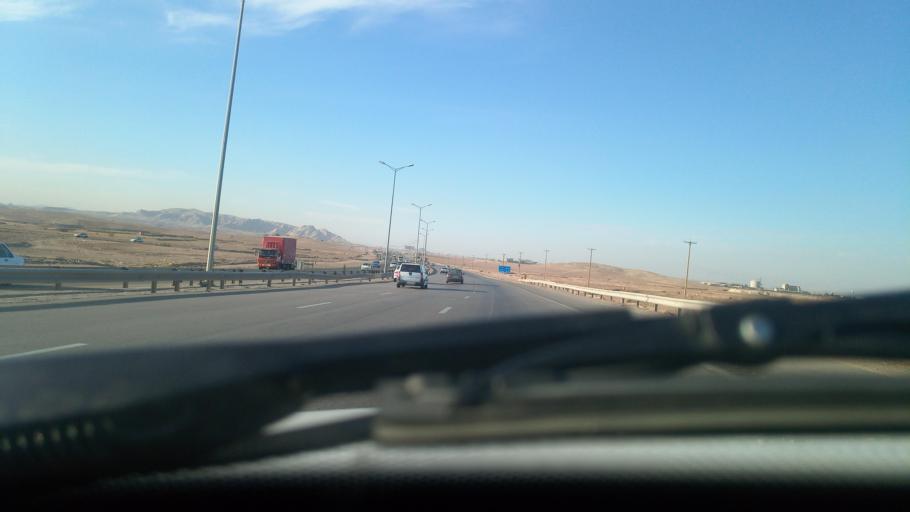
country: IR
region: Razavi Khorasan
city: Mashhad
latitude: 36.0849
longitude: 59.7412
